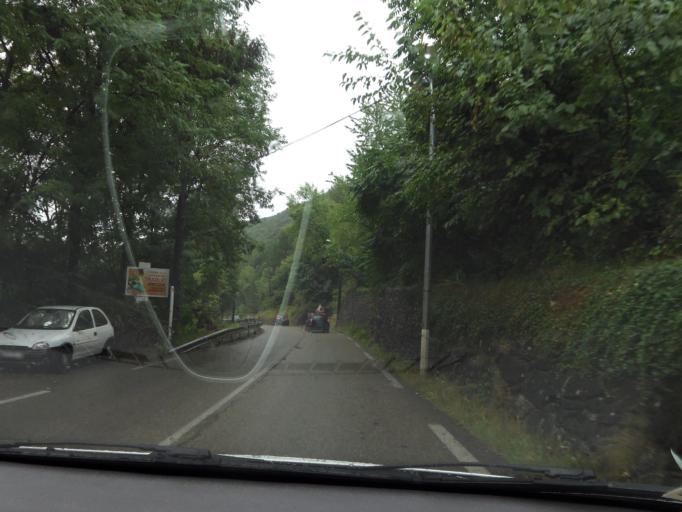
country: FR
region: Languedoc-Roussillon
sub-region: Departement du Gard
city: Les Salles-du-Gardon
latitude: 44.2078
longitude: 4.0238
